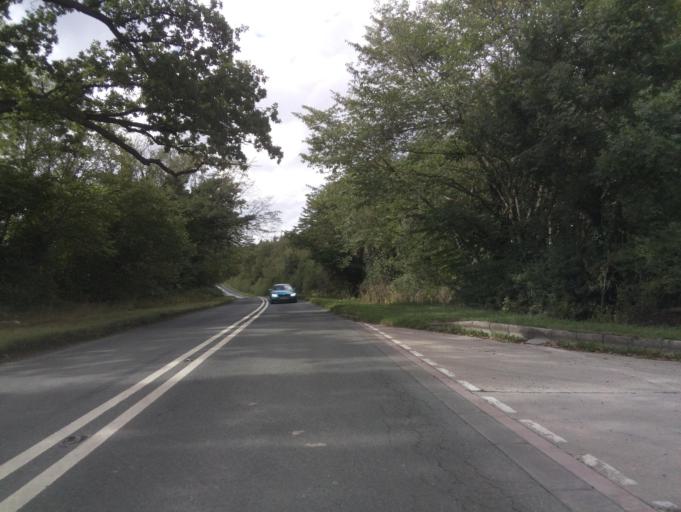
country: GB
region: England
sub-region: North Yorkshire
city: Bedale
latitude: 54.2366
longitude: -1.6756
